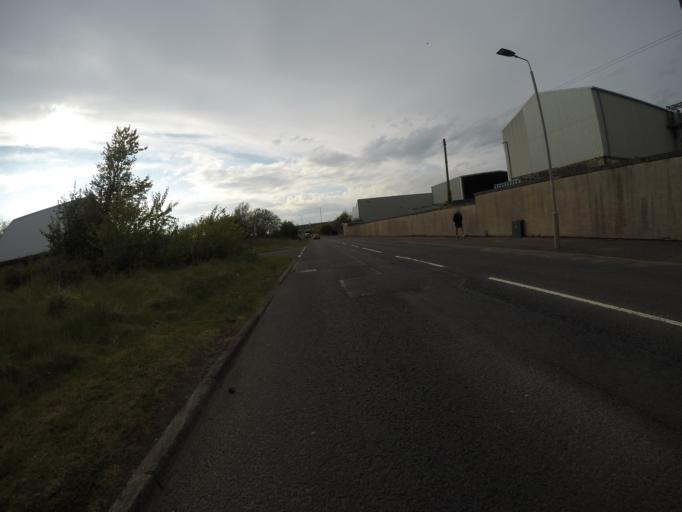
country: GB
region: Scotland
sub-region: North Ayrshire
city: Irvine
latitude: 55.6057
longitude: -4.6788
